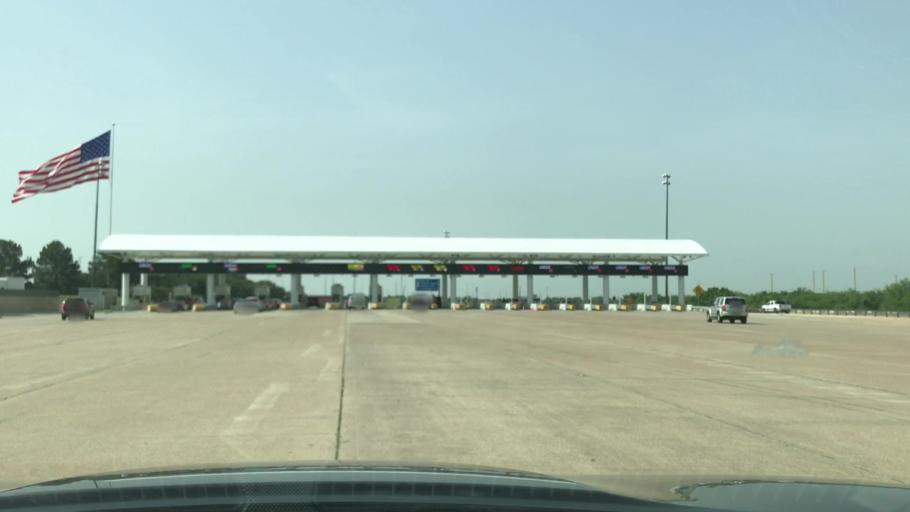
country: US
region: Texas
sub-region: Tarrant County
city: Euless
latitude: 32.8670
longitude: -97.0412
